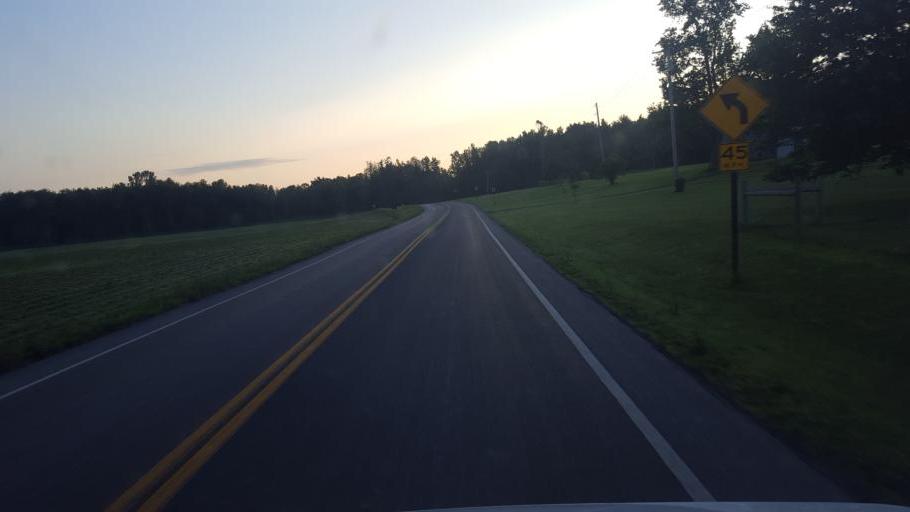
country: US
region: New York
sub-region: Wayne County
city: Clyde
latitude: 43.0644
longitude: -76.8920
